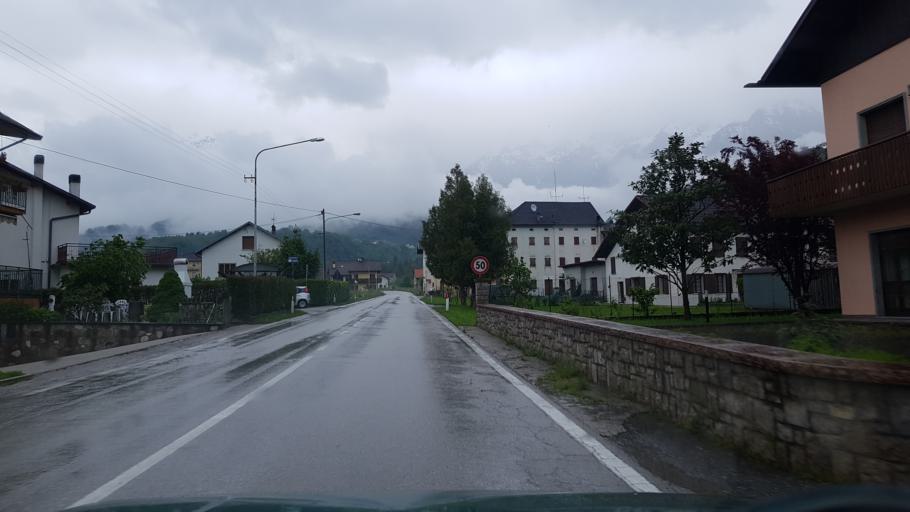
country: IT
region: Veneto
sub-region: Provincia di Belluno
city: Puos d'Alpago
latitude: 46.1444
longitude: 12.3826
